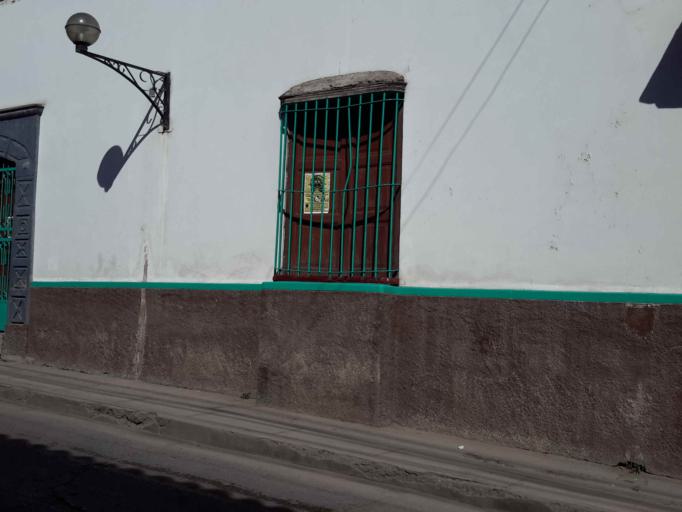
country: PE
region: Ayacucho
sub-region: Provincia de Huamanga
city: Ayacucho
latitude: -13.1664
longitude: -74.2276
